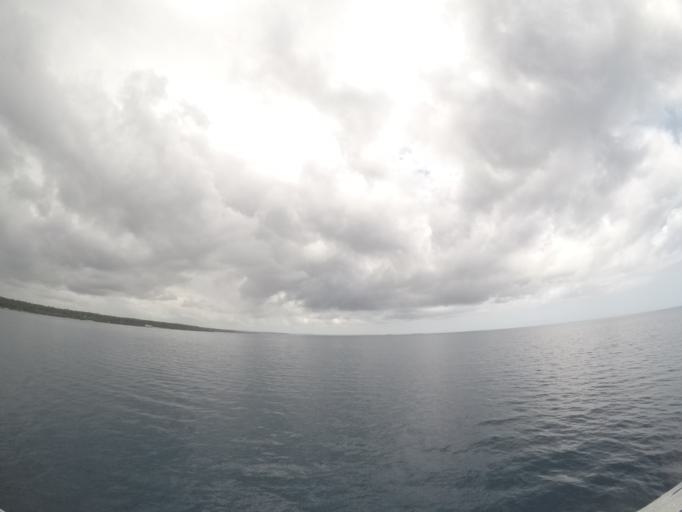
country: TZ
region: Zanzibar North
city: Mkokotoni
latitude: -5.9793
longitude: 39.1724
